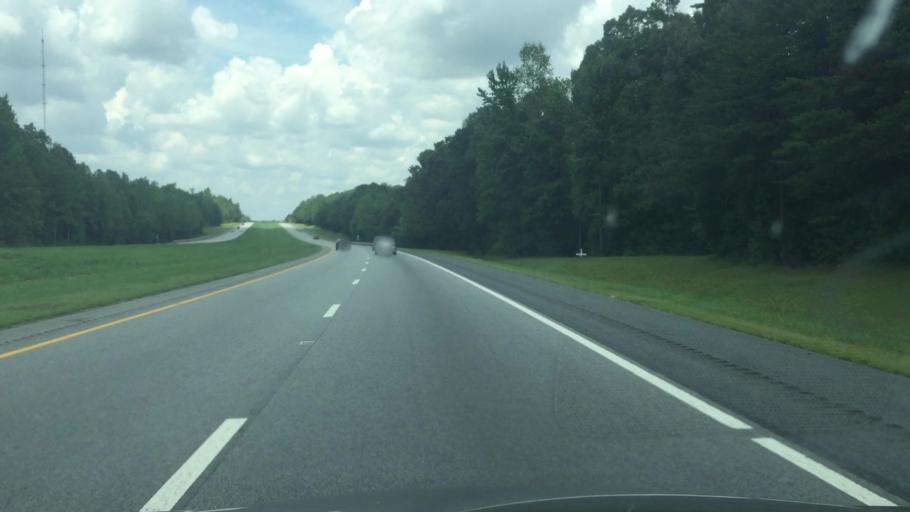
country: US
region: North Carolina
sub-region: Guilford County
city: Pleasant Garden
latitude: 35.9552
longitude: -79.8201
